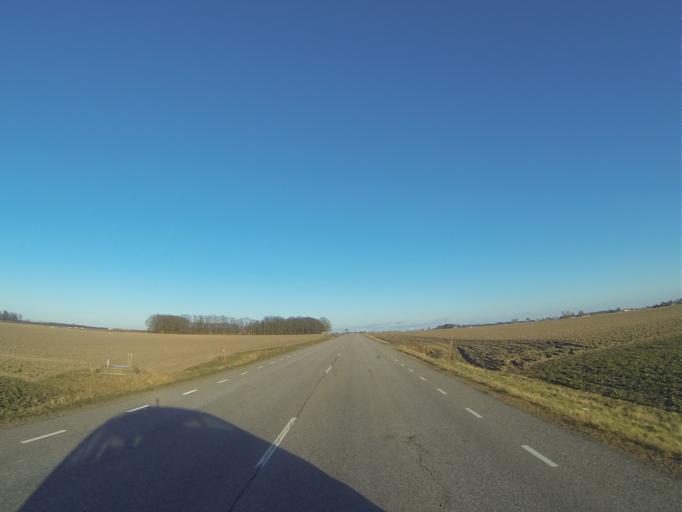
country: SE
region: Skane
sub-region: Malmo
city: Tygelsjo
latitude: 55.5438
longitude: 12.9935
